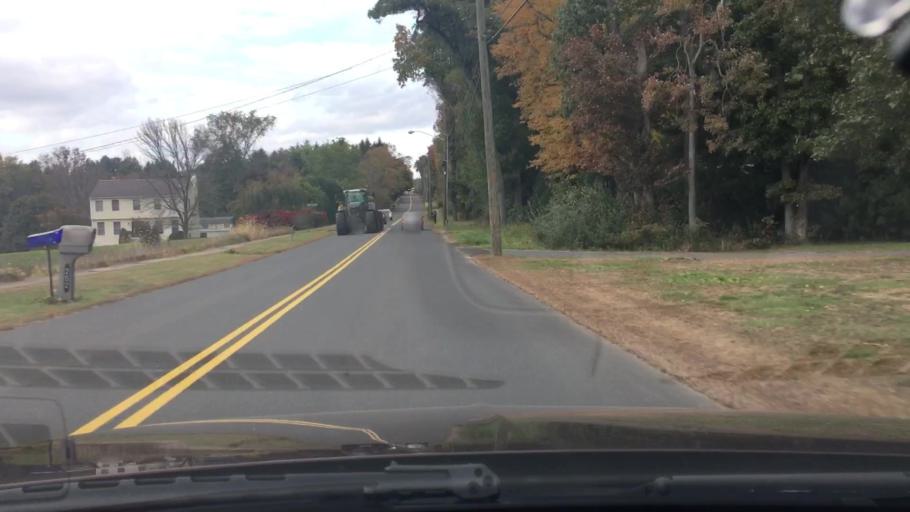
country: US
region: Connecticut
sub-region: Tolland County
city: Ellington
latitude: 41.9307
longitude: -72.4779
